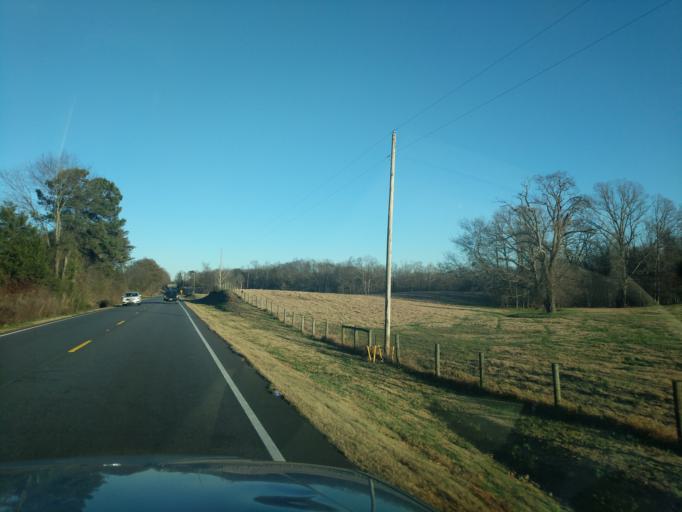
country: US
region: South Carolina
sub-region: Oconee County
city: Utica
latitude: 34.5839
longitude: -82.9374
